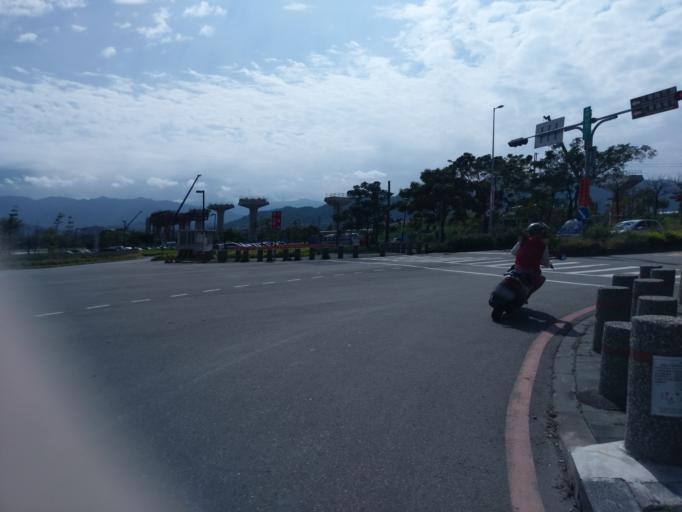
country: TW
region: Taiwan
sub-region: Taoyuan
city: Taoyuan
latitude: 24.9554
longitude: 121.3590
